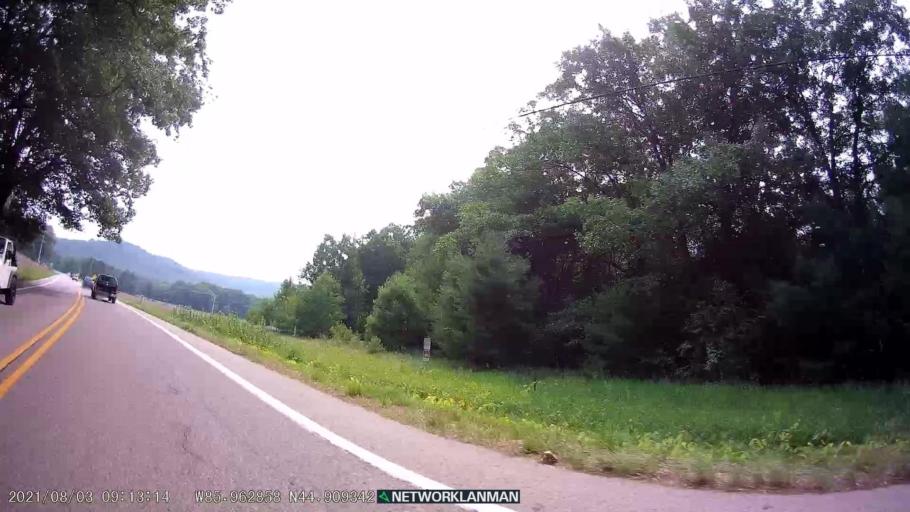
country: US
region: Michigan
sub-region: Leelanau County
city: Leland
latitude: 44.9094
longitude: -85.9627
